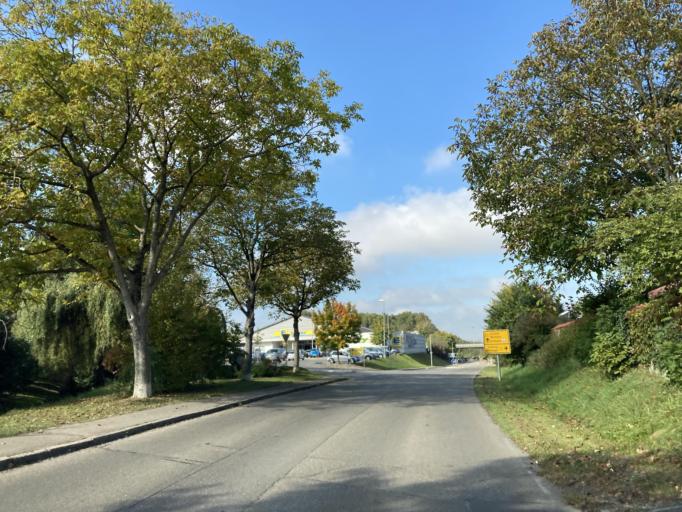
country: DE
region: Baden-Wuerttemberg
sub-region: Freiburg Region
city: Buggingen
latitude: 47.8518
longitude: 7.6349
